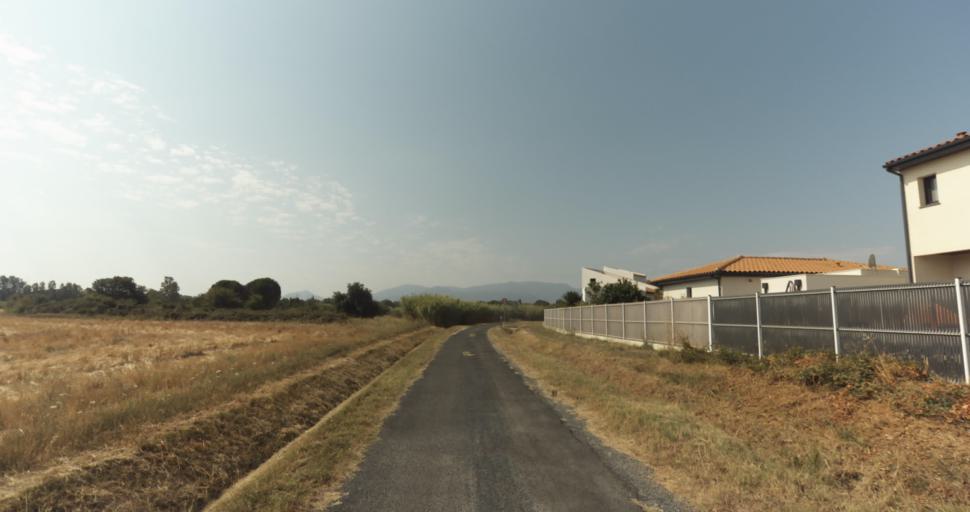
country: FR
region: Languedoc-Roussillon
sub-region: Departement des Pyrenees-Orientales
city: Latour-Bas-Elne
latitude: 42.6149
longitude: 3.0167
